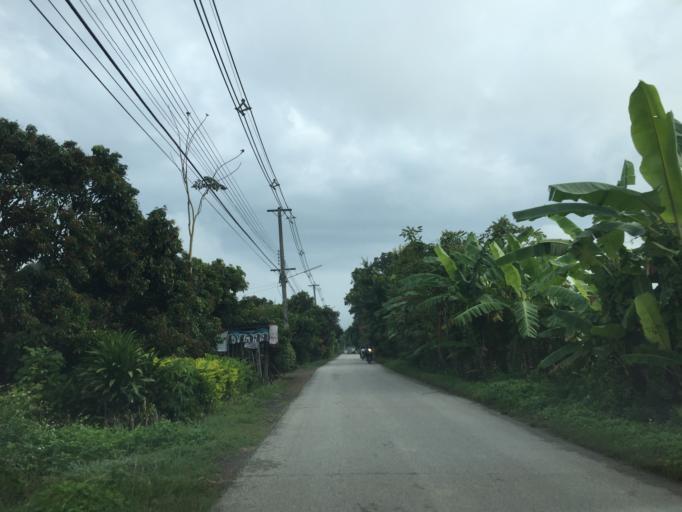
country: TH
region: Lamphun
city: Ban Thi
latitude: 18.6506
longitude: 99.0624
